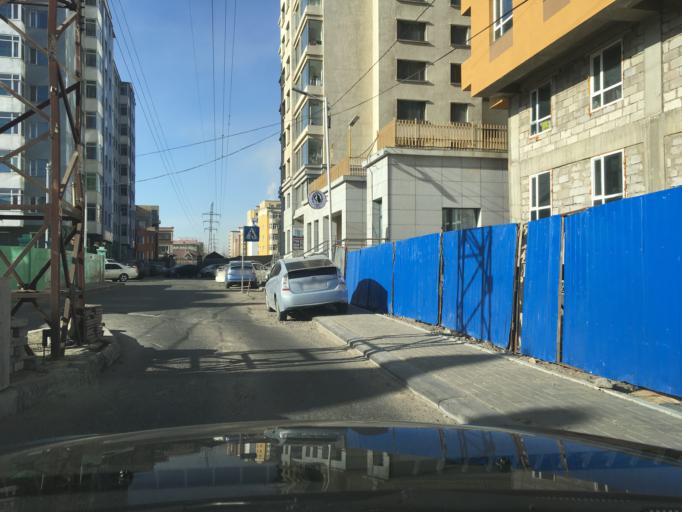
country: MN
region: Ulaanbaatar
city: Ulaanbaatar
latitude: 47.8926
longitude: 106.9073
